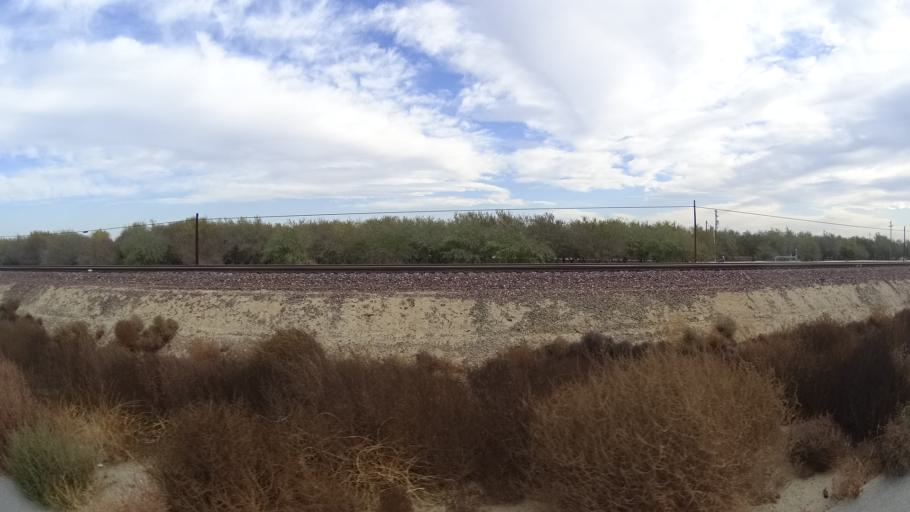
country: US
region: California
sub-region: Kern County
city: Rosedale
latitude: 35.4347
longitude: -119.1907
